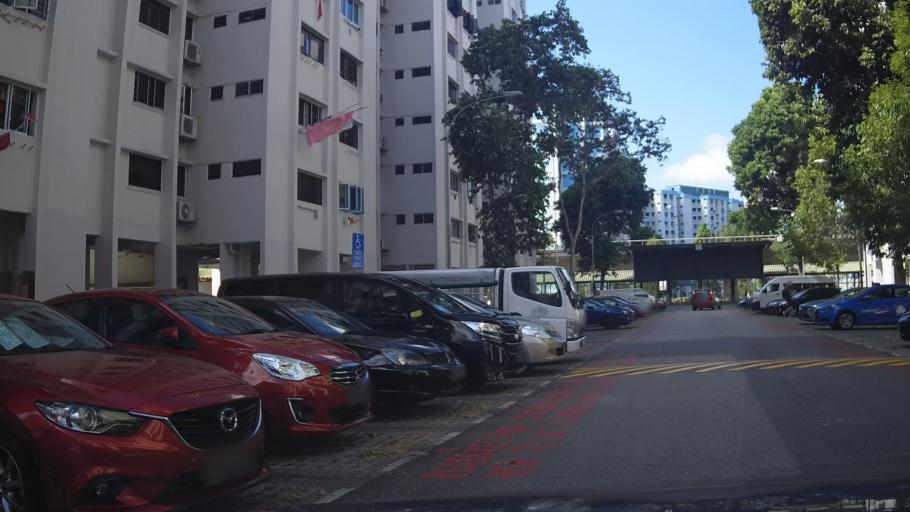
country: SG
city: Singapore
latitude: 1.3522
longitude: 103.9472
